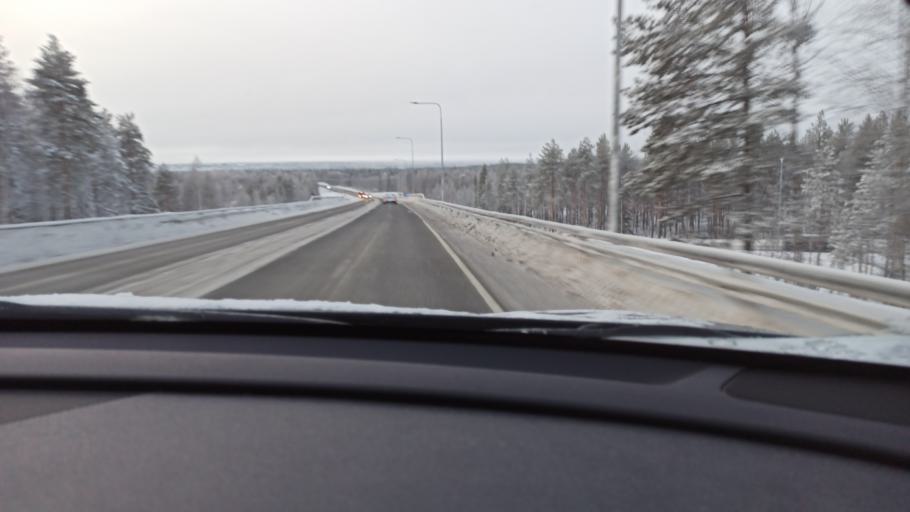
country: FI
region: Lapland
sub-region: Rovaniemi
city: Rovaniemi
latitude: 66.5369
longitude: 25.7810
